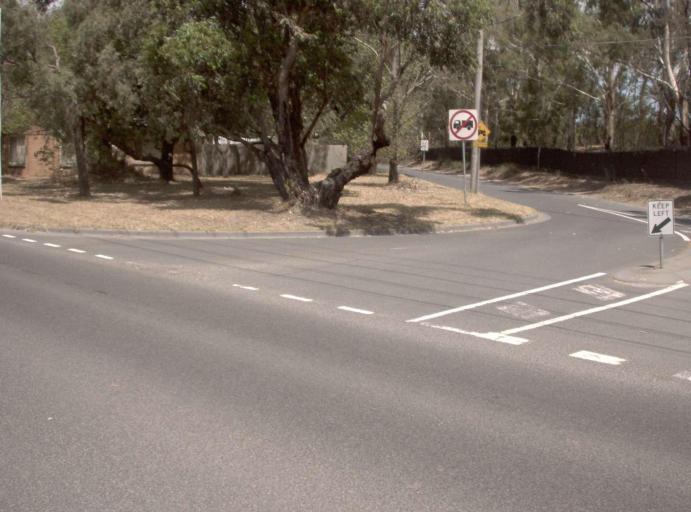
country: AU
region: Victoria
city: Heatherton
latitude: -37.9653
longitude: 145.1065
